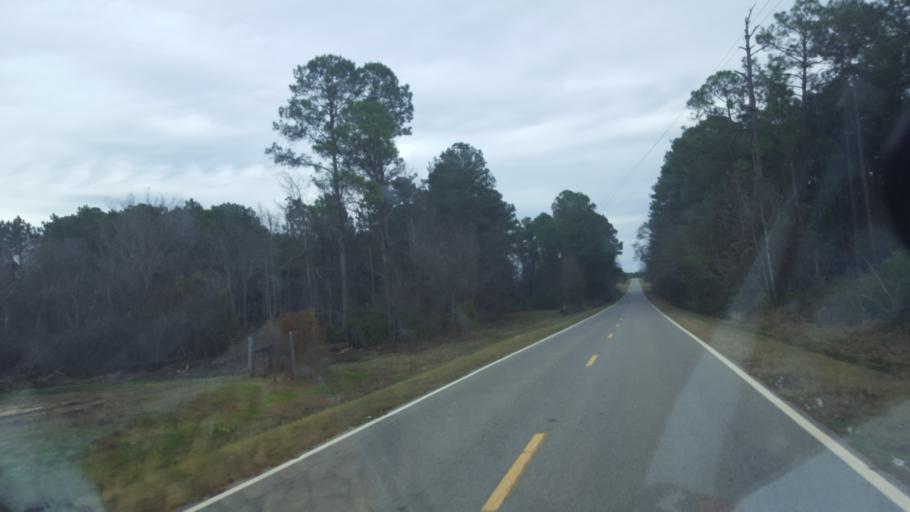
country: US
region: Georgia
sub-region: Ben Hill County
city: Fitzgerald
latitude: 31.7700
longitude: -83.3678
